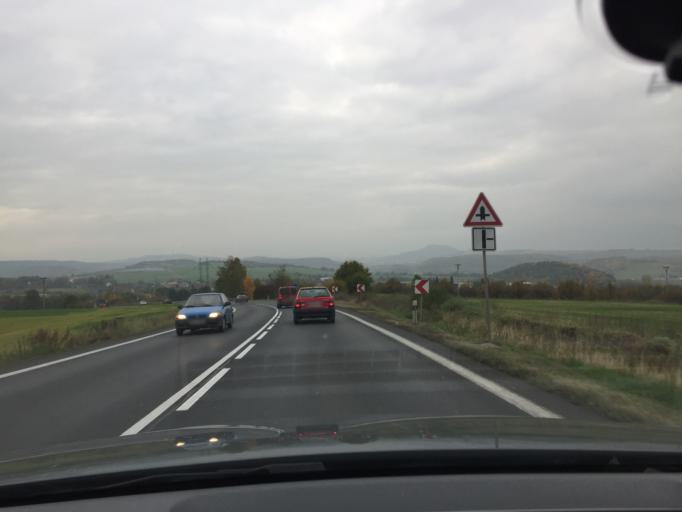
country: CZ
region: Ustecky
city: Rehlovice
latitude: 50.5832
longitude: 13.9233
